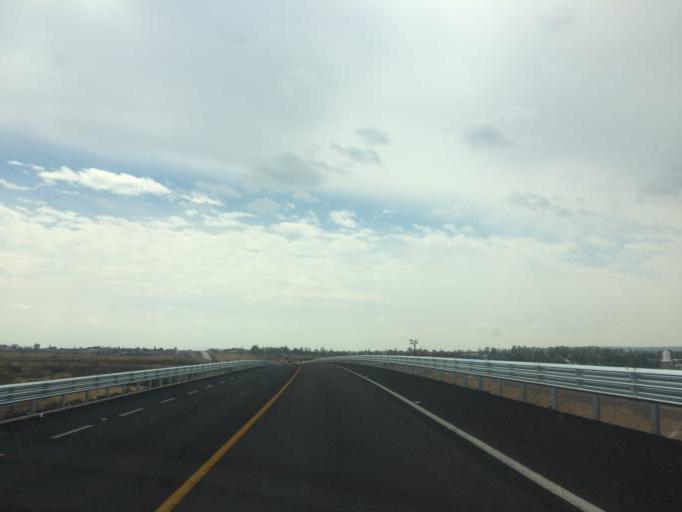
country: MX
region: Guanajuato
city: Duarte
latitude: 21.0513
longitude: -101.5287
